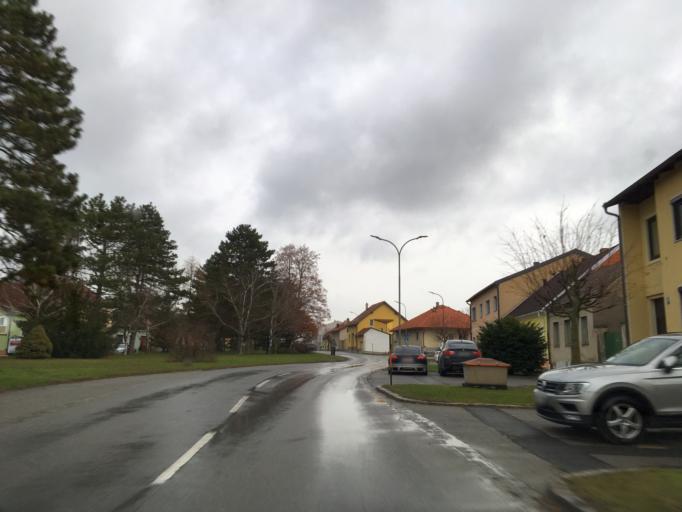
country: AT
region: Lower Austria
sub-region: Politischer Bezirk Wien-Umgebung
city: Rauchenwarth
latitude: 48.0829
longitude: 16.5322
